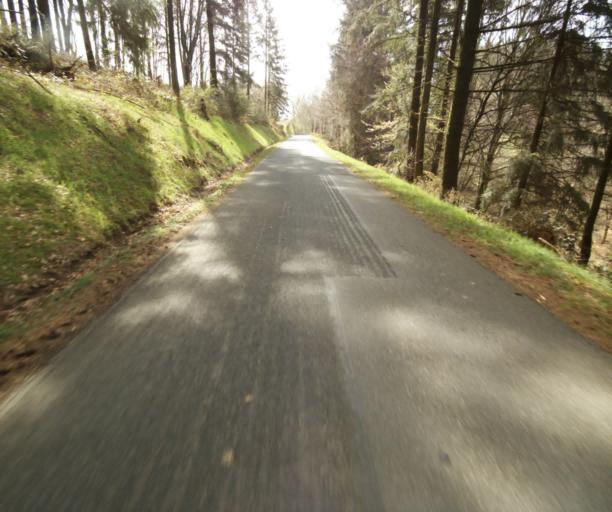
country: FR
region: Limousin
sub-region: Departement de la Correze
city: Correze
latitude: 45.3722
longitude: 1.9027
